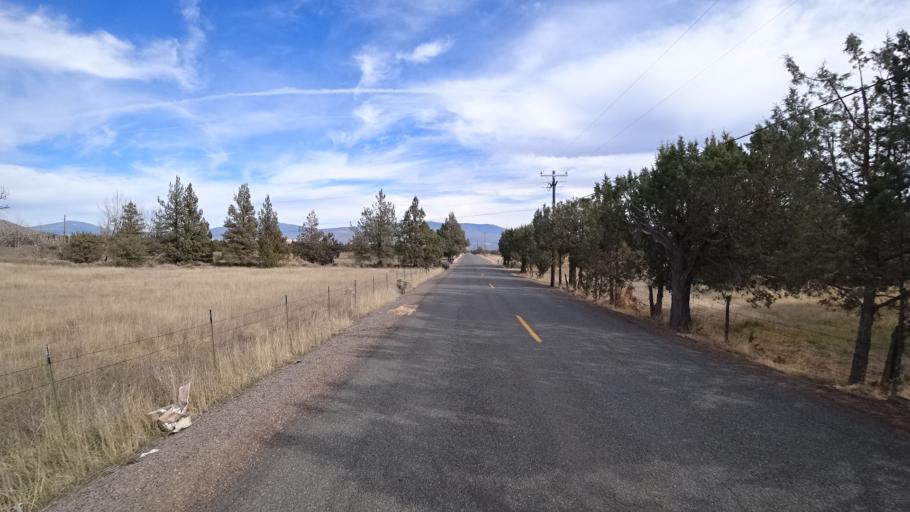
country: US
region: California
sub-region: Siskiyou County
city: Montague
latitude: 41.6384
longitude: -122.4084
